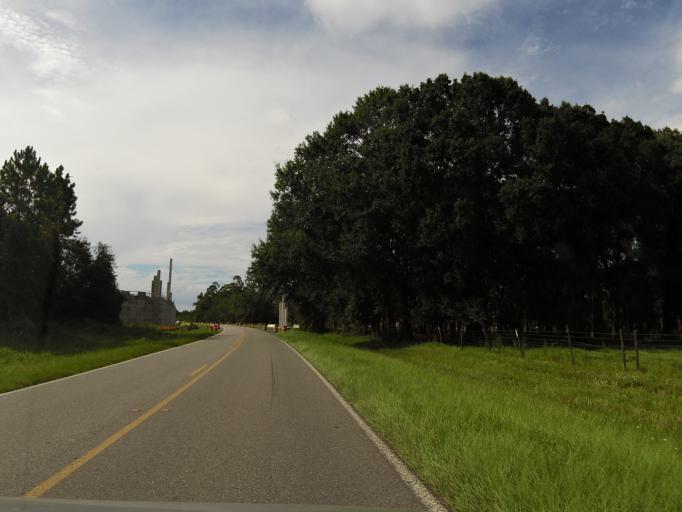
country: US
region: Florida
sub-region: Clay County
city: Green Cove Springs
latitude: 29.9527
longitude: -81.6658
